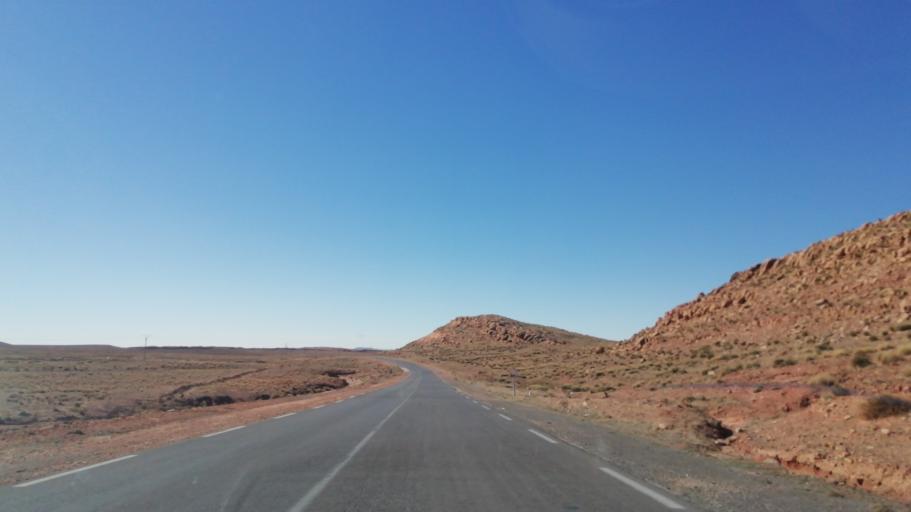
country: DZ
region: El Bayadh
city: El Bayadh
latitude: 33.6549
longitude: 1.4130
